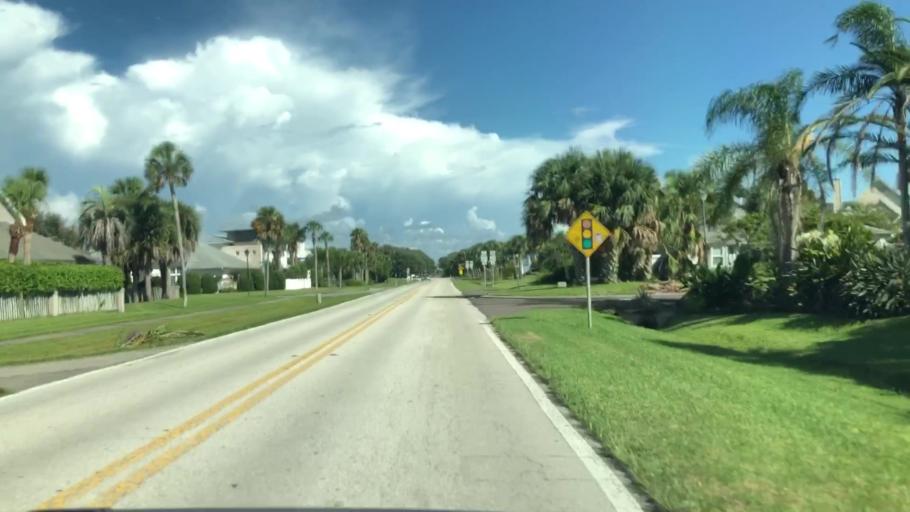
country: US
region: Florida
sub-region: Saint Johns County
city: Ponte Vedra Beach
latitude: 30.2586
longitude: -81.3851
